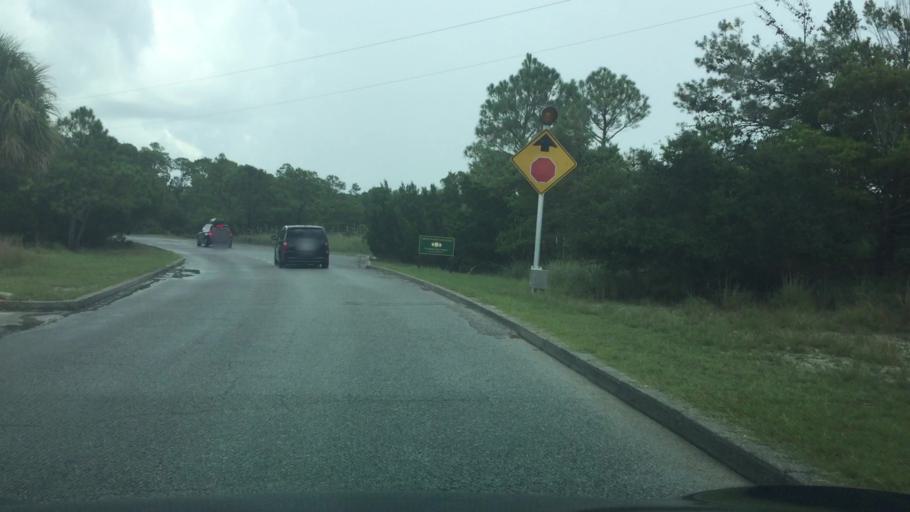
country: US
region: Florida
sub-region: Bay County
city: Lower Grand Lagoon
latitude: 30.1347
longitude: -85.7440
